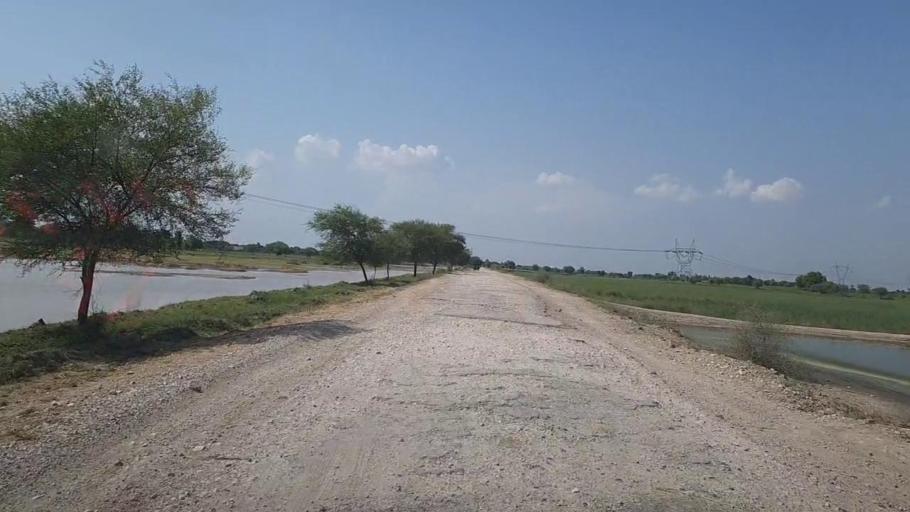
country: PK
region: Sindh
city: Khairpur
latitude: 28.1062
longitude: 69.6229
